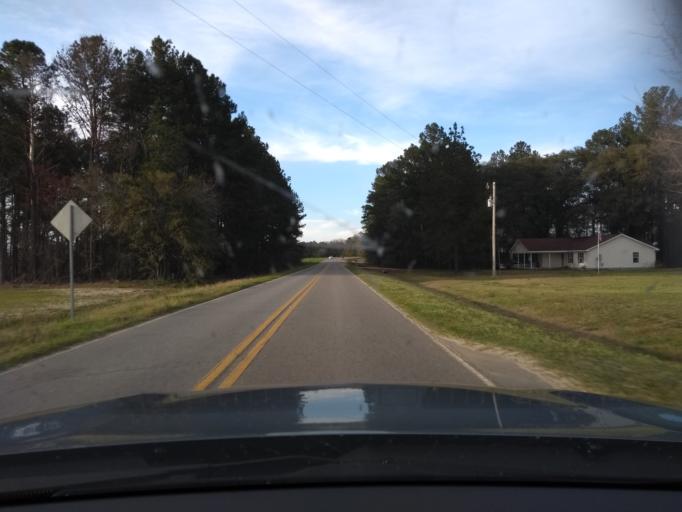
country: US
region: Georgia
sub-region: Evans County
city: Claxton
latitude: 32.2428
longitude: -81.7695
